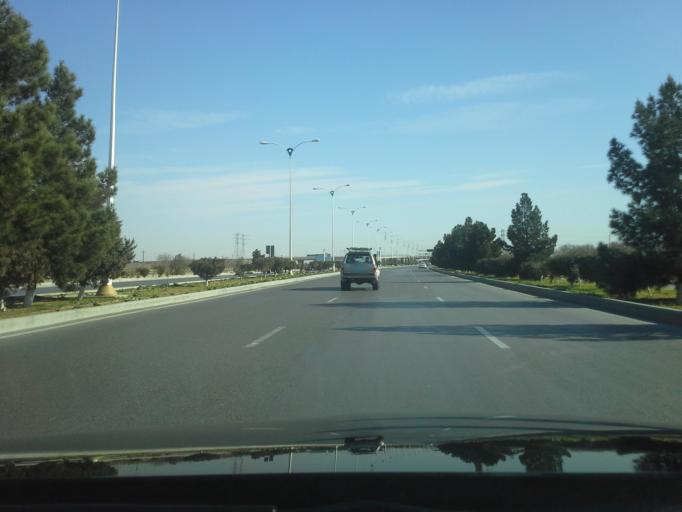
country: TM
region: Ahal
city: Annau
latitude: 37.9152
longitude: 58.4761
